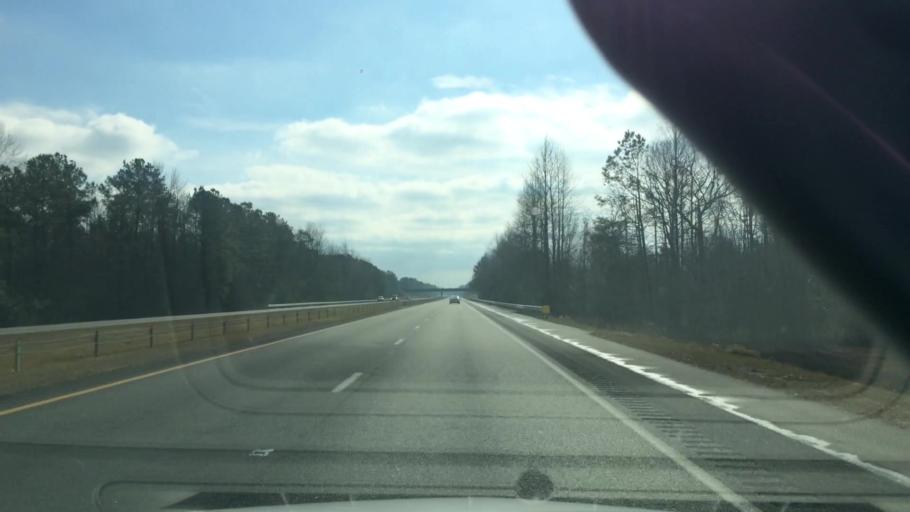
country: US
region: North Carolina
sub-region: Pender County
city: Rocky Point
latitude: 34.4861
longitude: -77.8782
